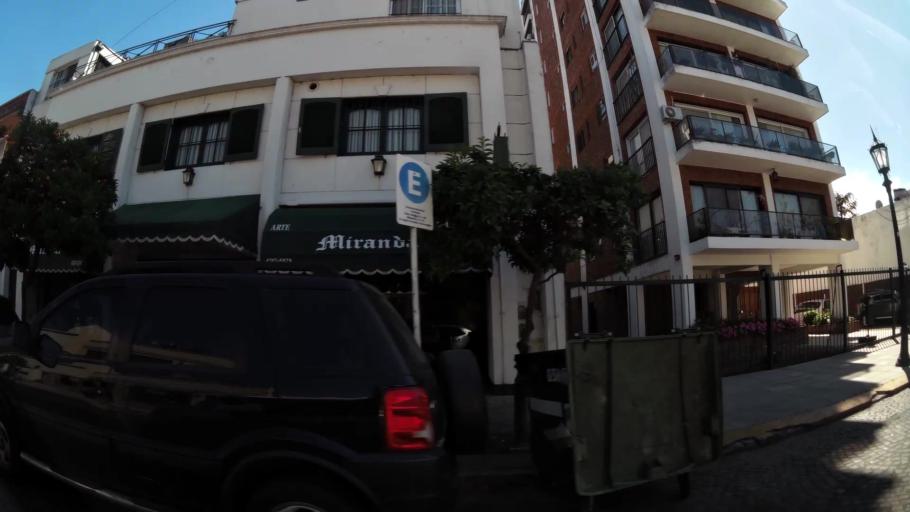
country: AR
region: Buenos Aires
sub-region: Partido de San Isidro
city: San Isidro
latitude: -34.4695
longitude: -58.5091
